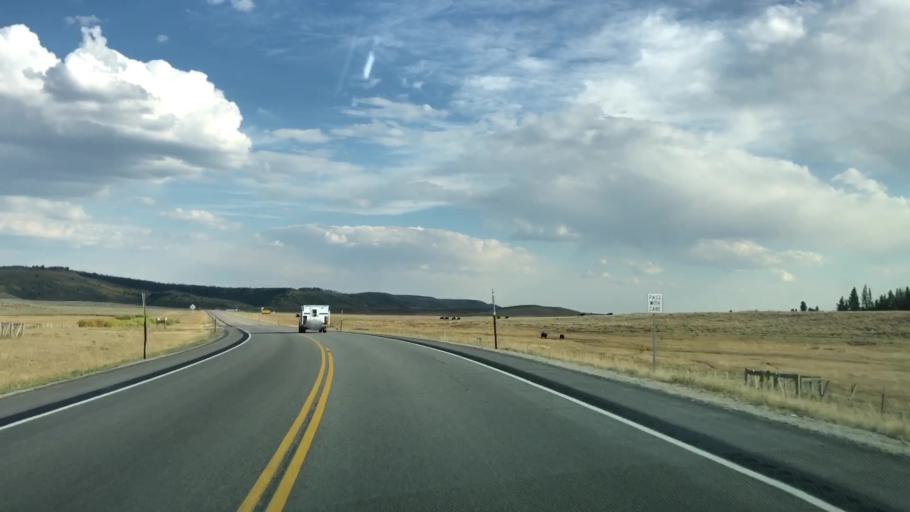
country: US
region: Wyoming
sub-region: Sublette County
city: Pinedale
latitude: 43.1262
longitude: -110.1893
